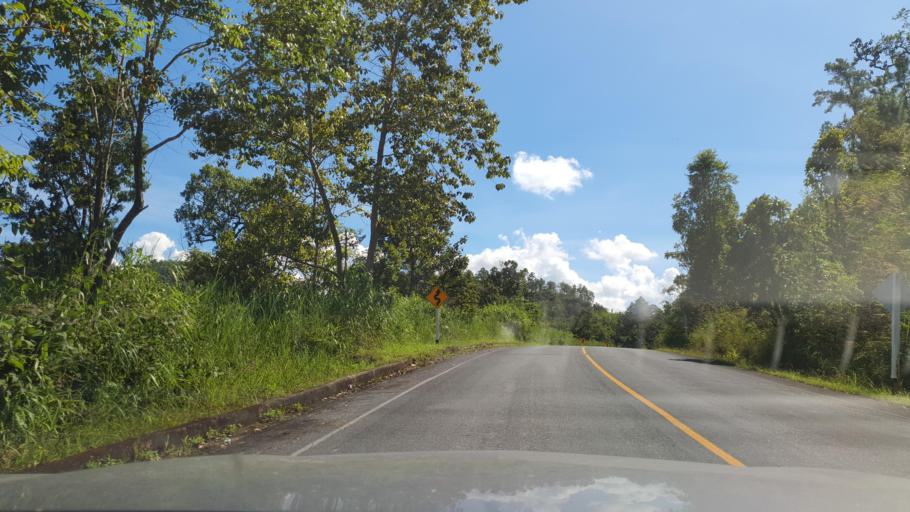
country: TH
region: Chiang Mai
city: Phrao
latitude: 19.3538
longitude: 99.2764
